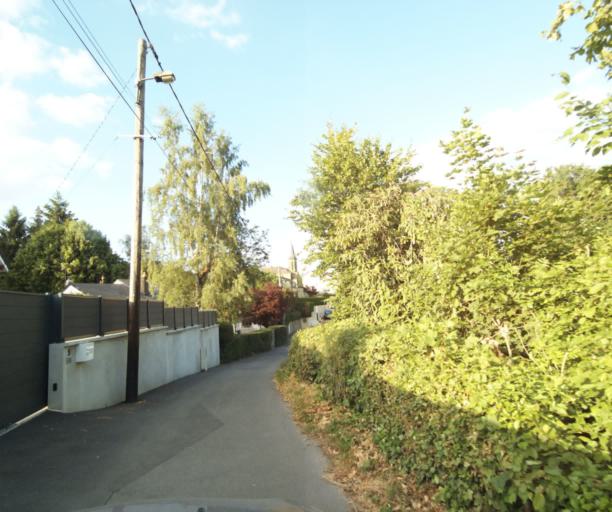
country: FR
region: Champagne-Ardenne
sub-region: Departement des Ardennes
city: Charleville-Mezieres
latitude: 49.7853
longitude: 4.7219
